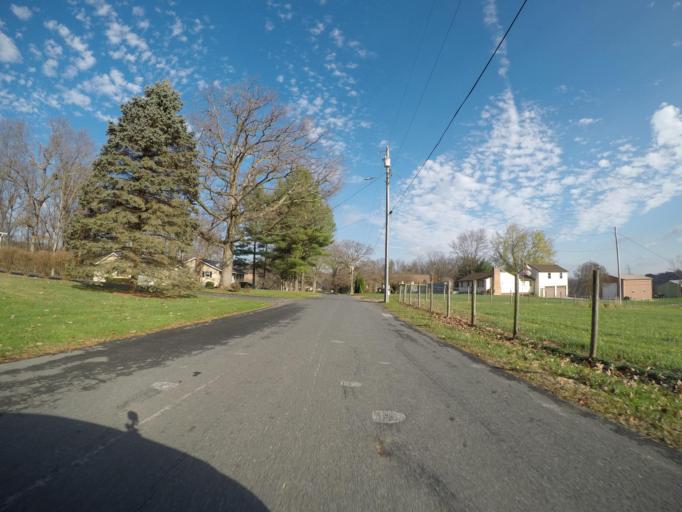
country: US
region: Maryland
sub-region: Carroll County
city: Hampstead
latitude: 39.5616
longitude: -76.8165
